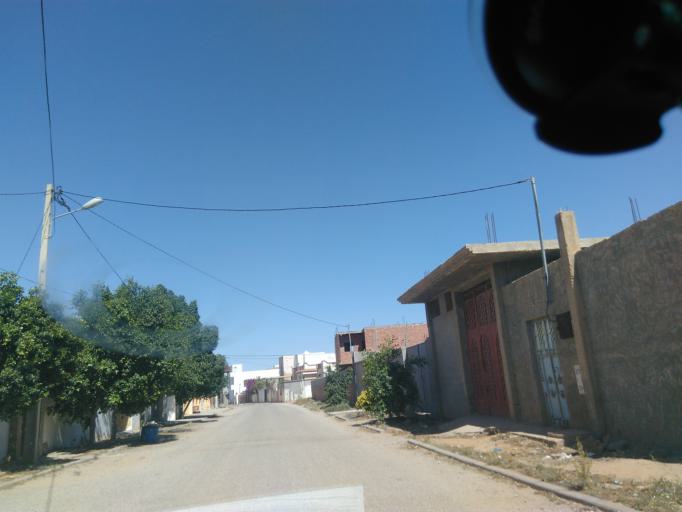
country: TN
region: Tataouine
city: Tataouine
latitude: 32.9487
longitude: 10.4680
